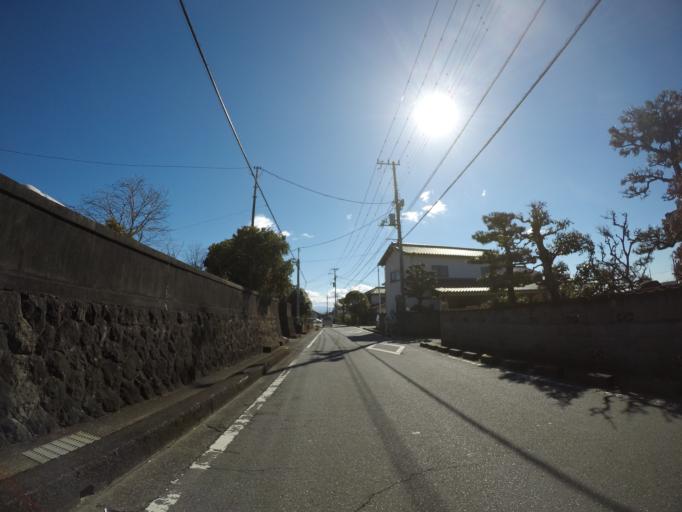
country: JP
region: Shizuoka
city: Fuji
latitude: 35.1513
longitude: 138.7670
